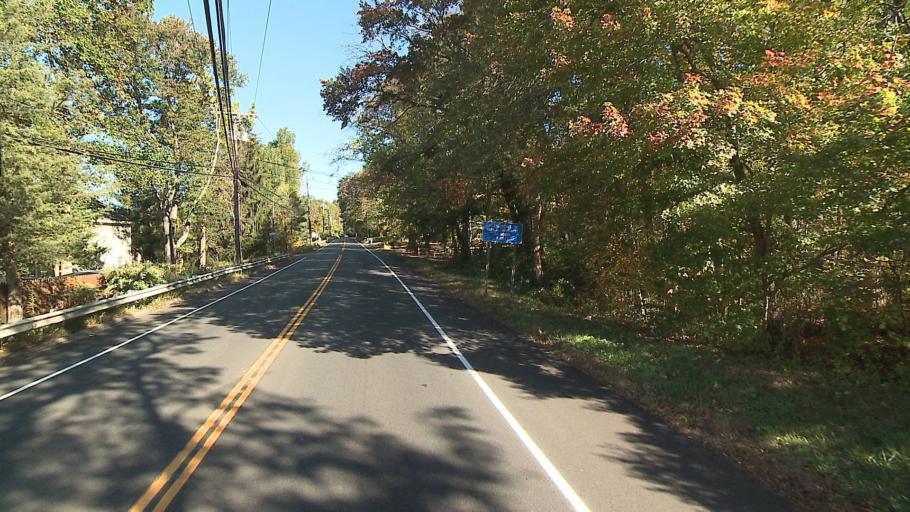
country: US
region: Connecticut
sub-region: Middlesex County
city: Lake Pocotopaug
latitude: 41.5942
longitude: -72.4899
